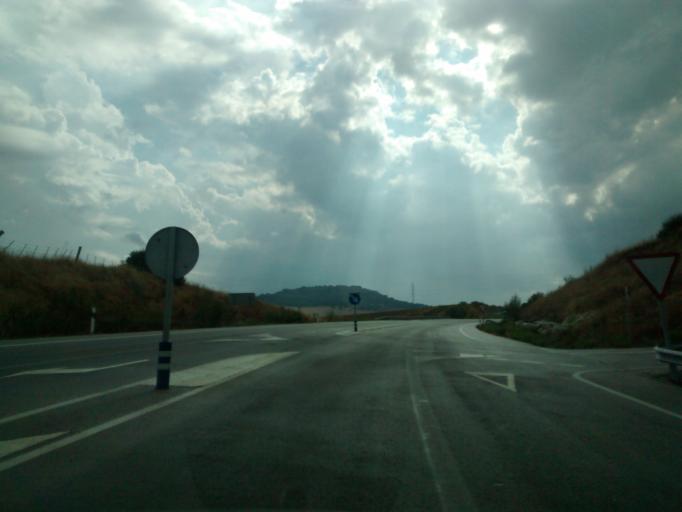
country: ES
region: Andalusia
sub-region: Provincia de Cadiz
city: El Bosque
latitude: 36.7520
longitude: -5.5259
